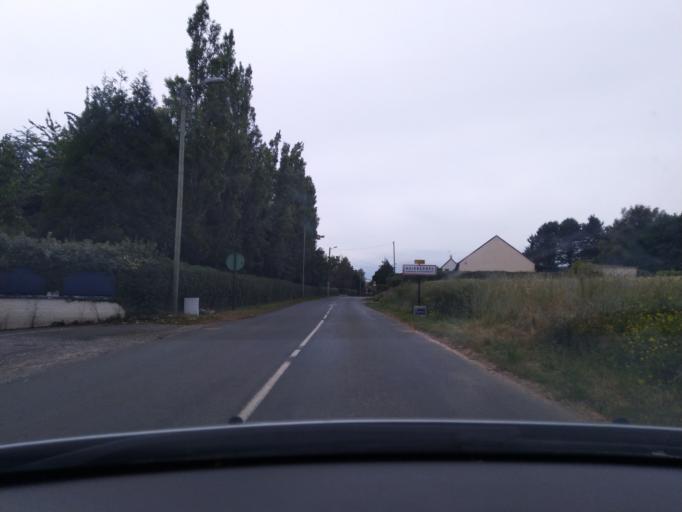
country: FR
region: Nord-Pas-de-Calais
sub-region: Departement du Pas-de-Calais
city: Marquise
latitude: 50.8428
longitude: 1.6832
